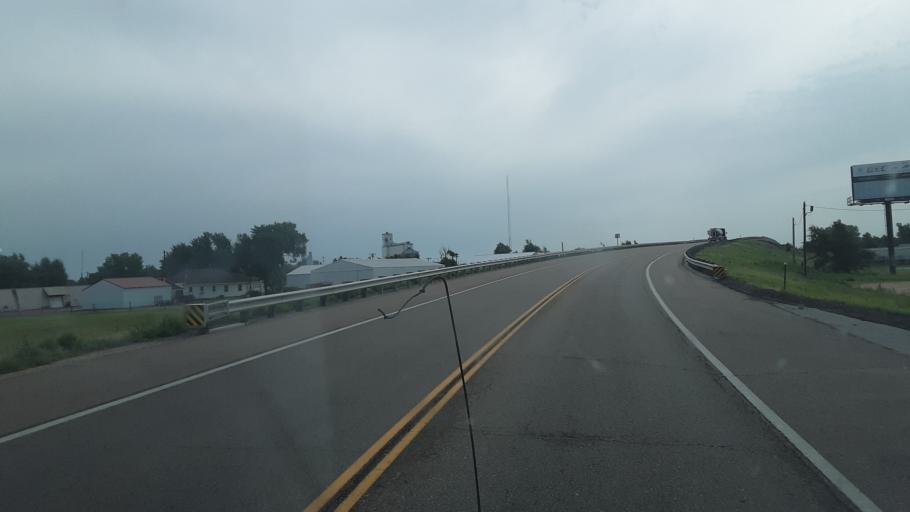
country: US
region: Kansas
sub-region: Edwards County
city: Kinsley
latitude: 37.9185
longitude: -99.4221
